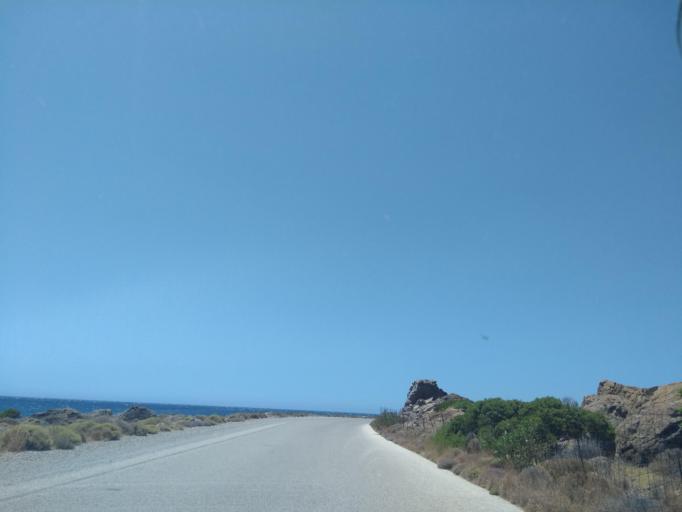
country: GR
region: Crete
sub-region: Nomos Chanias
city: Vryses
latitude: 35.3506
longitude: 23.5376
